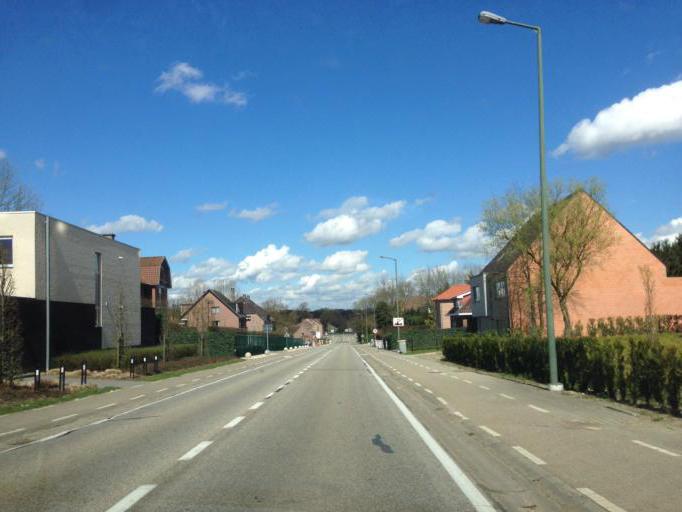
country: BE
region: Flanders
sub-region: Provincie Limburg
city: As
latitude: 51.0085
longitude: 5.5834
